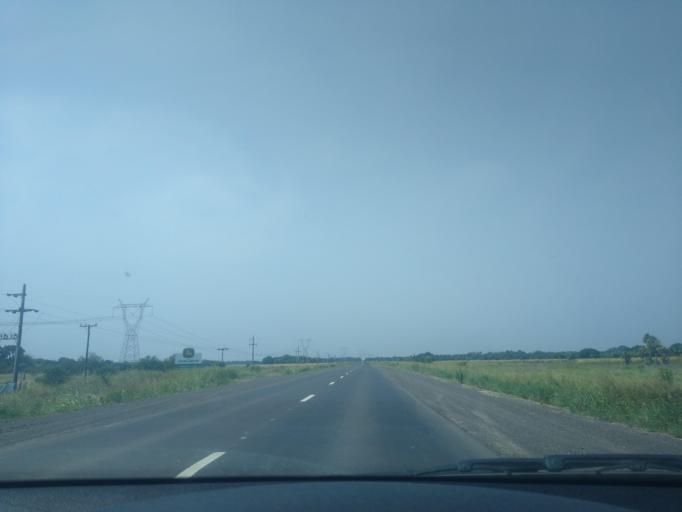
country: AR
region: Chaco
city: Fontana
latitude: -27.5679
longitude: -59.1533
